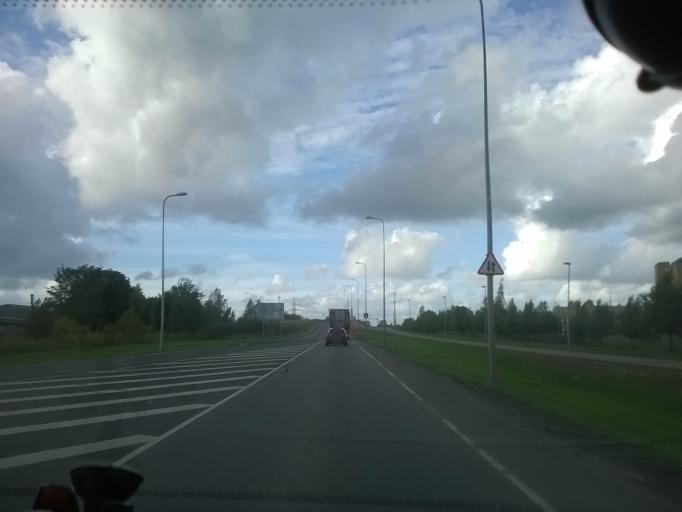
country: EE
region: Harju
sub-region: Tallinna linn
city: Kose
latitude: 59.4179
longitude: 24.8440
